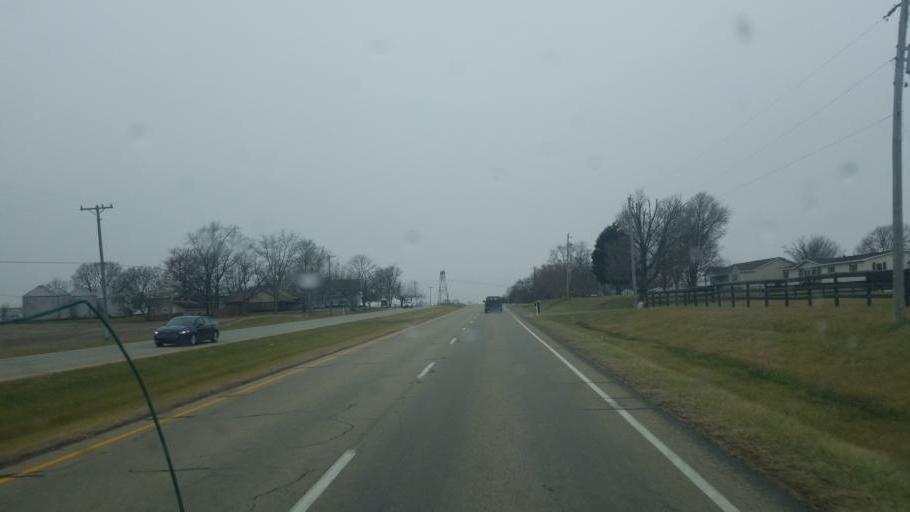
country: US
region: Indiana
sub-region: Hancock County
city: Greenfield
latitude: 39.7901
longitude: -85.6568
